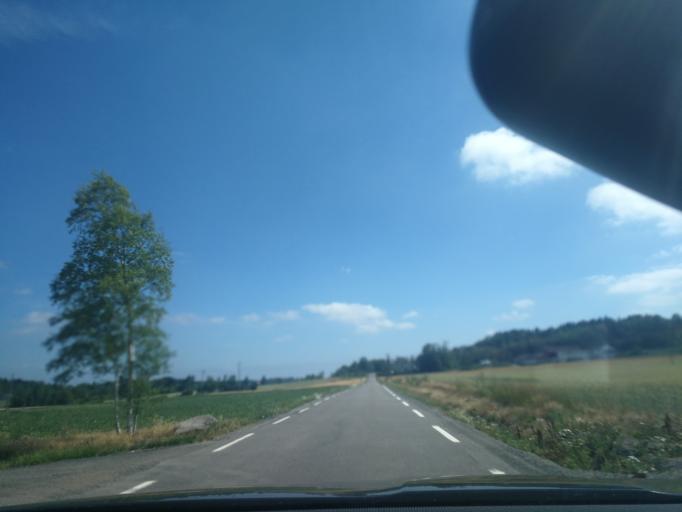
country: NO
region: Vestfold
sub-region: Stokke
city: Stokke
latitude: 59.2075
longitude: 10.2679
